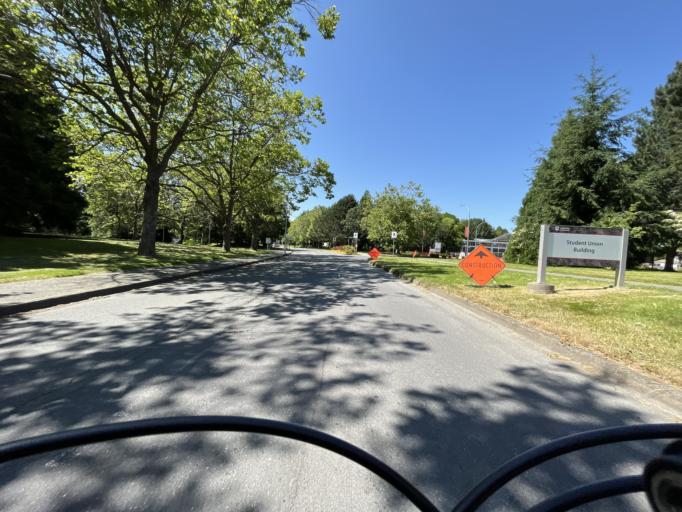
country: CA
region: British Columbia
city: Oak Bay
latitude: 48.4650
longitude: -123.3091
